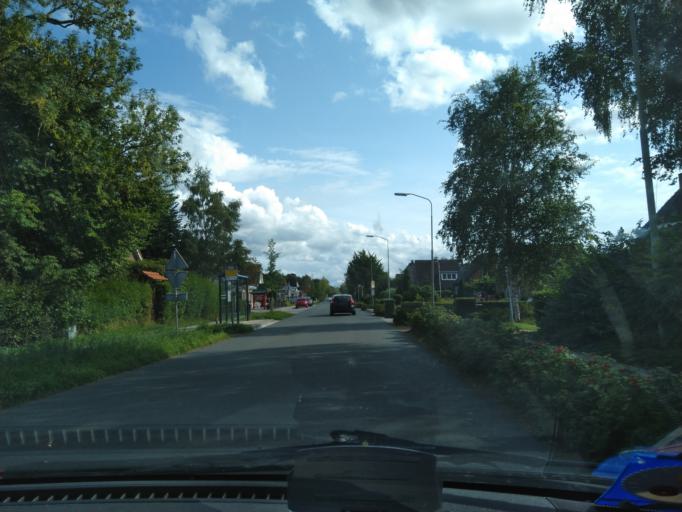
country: NL
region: Groningen
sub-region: Gemeente Groningen
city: Groningen
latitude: 53.1771
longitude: 6.5437
